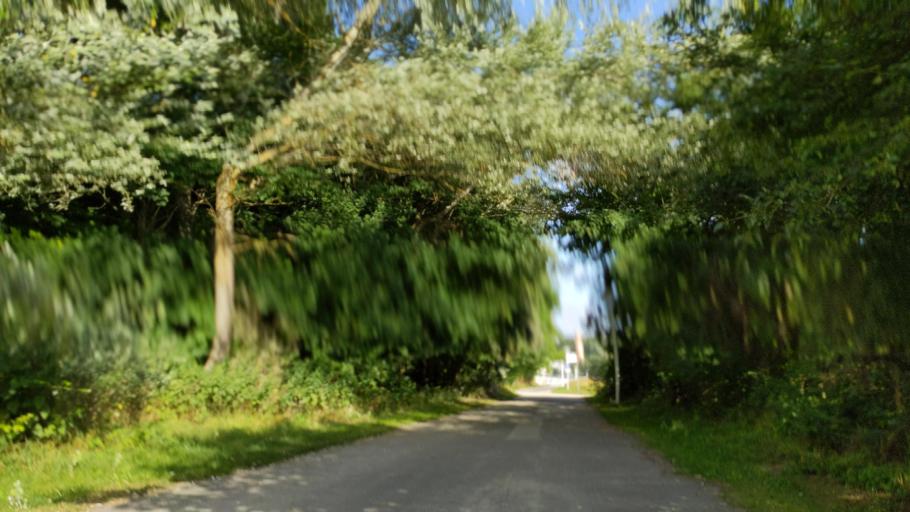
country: DE
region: Schleswig-Holstein
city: Travemuende
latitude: 53.9570
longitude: 10.8859
